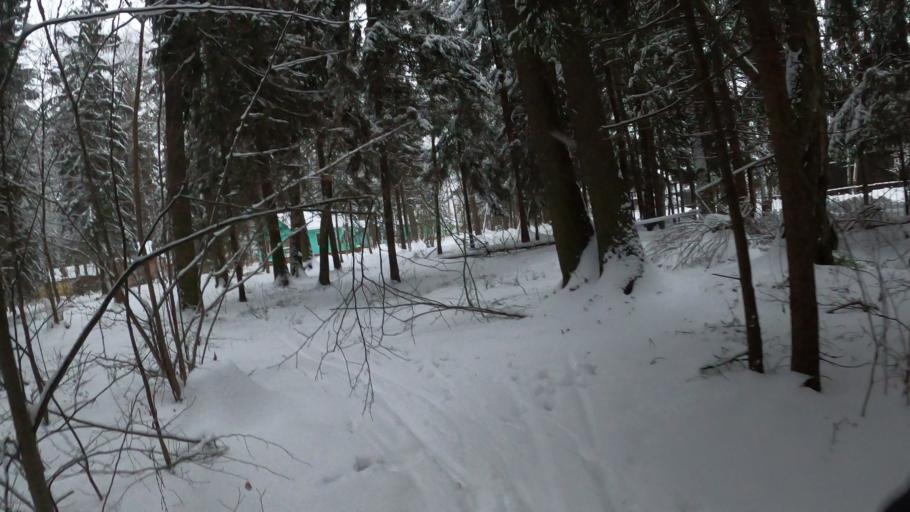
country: RU
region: Moskovskaya
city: Firsanovka
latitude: 55.9138
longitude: 37.2040
